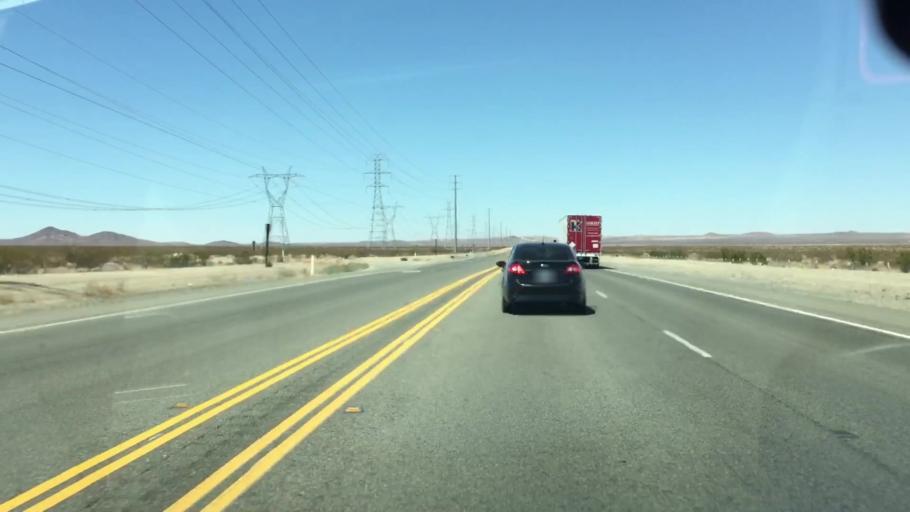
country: US
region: California
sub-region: San Bernardino County
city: Adelanto
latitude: 34.7617
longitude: -117.4743
